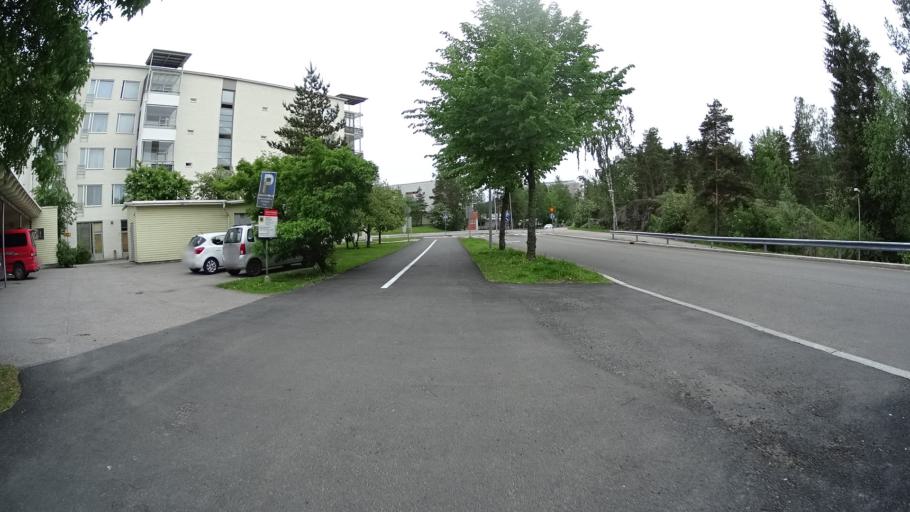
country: FI
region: Uusimaa
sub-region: Helsinki
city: Vantaa
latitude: 60.2442
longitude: 25.0750
